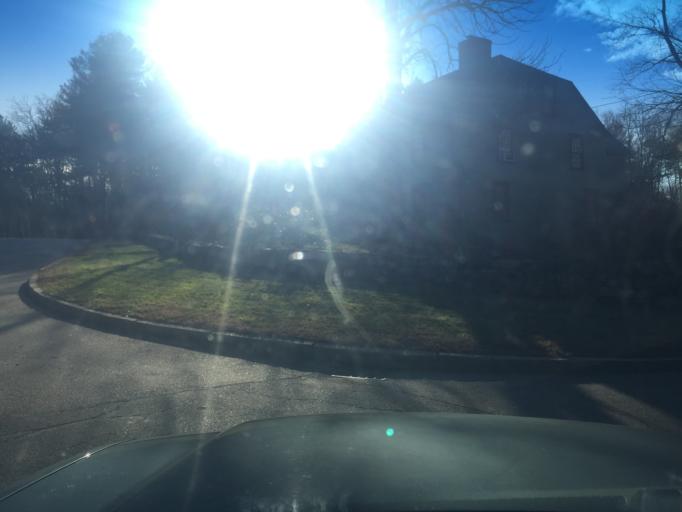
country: US
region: Massachusetts
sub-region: Middlesex County
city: Holliston
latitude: 42.2037
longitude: -71.4603
